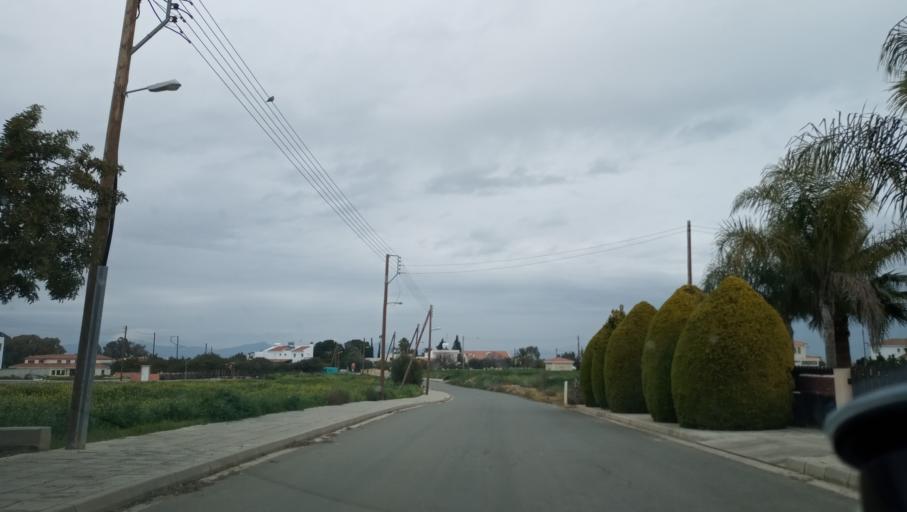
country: CY
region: Lefkosia
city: Kato Deftera
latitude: 35.0812
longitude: 33.2825
